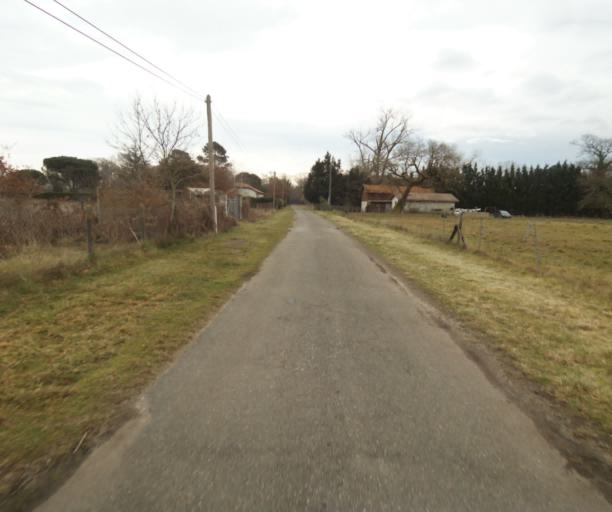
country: FR
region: Aquitaine
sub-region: Departement des Landes
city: Gabarret
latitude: 44.0150
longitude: -0.0559
